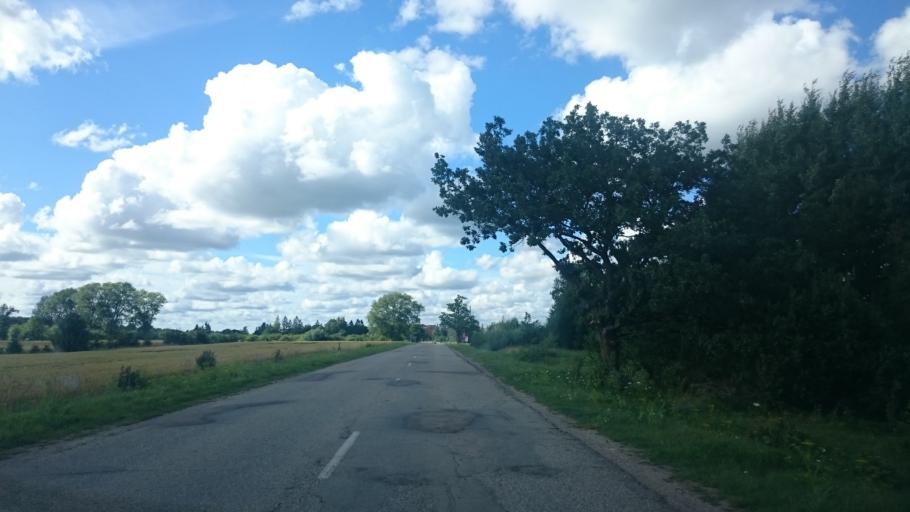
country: LV
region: Aizpute
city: Aizpute
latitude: 56.7021
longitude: 21.6276
